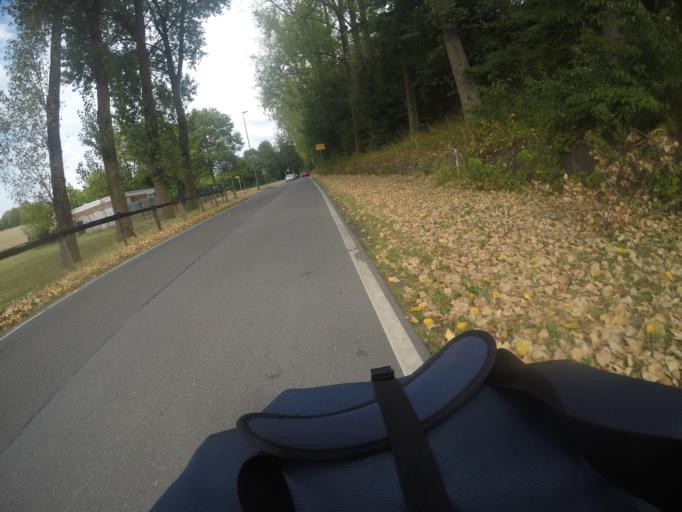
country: DE
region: North Rhine-Westphalia
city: Haan
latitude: 51.2227
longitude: 7.0471
